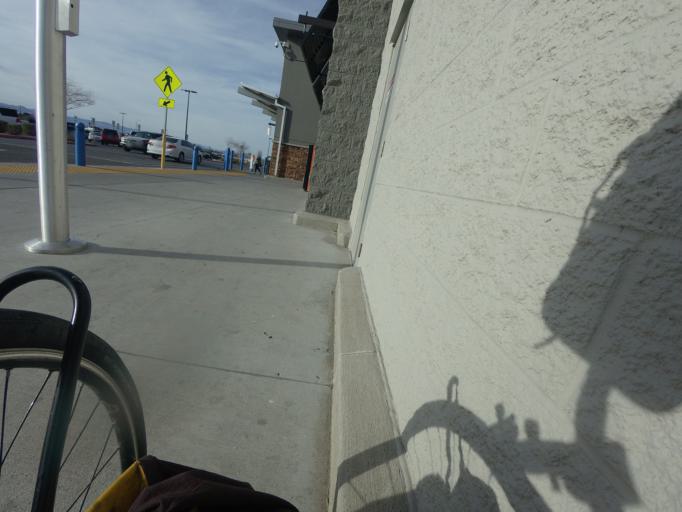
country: US
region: California
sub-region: Kern County
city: Ridgecrest
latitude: 35.6066
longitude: -117.6676
